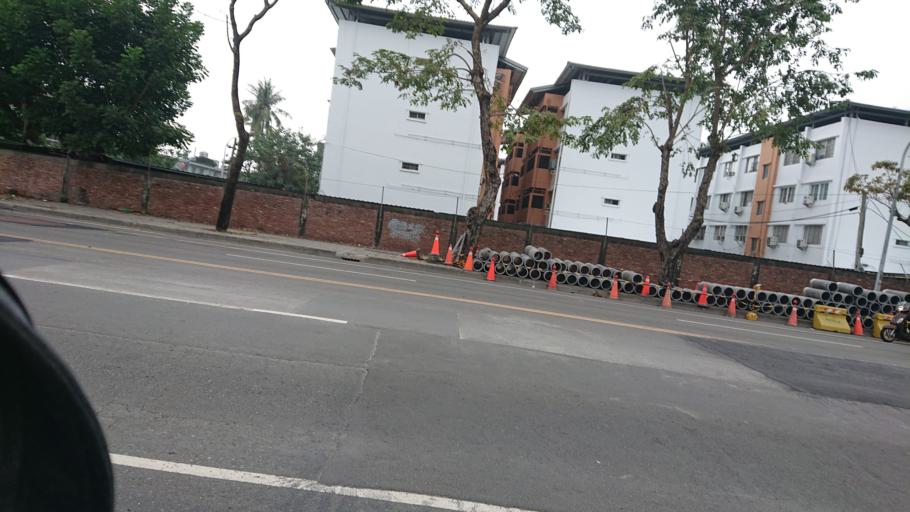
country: TW
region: Kaohsiung
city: Kaohsiung
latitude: 22.7035
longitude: 120.2926
